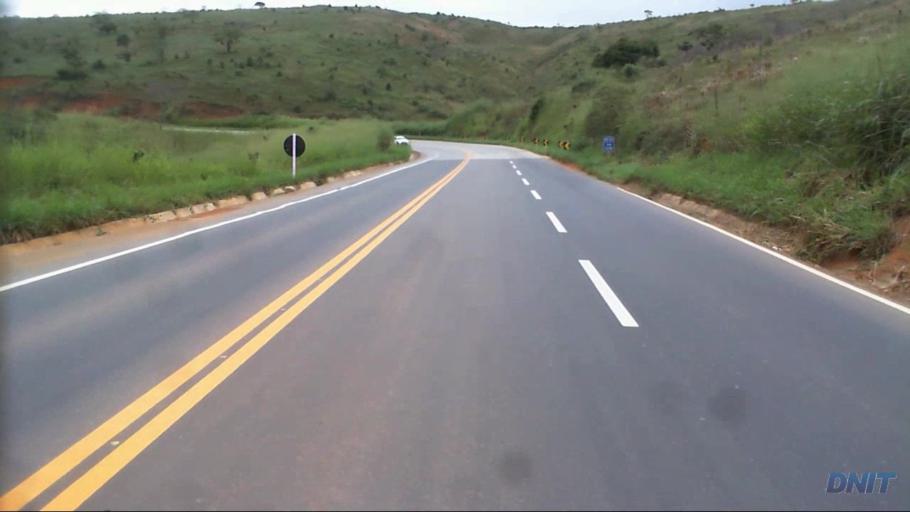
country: BR
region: Minas Gerais
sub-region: Nova Era
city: Nova Era
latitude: -19.7969
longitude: -43.0541
